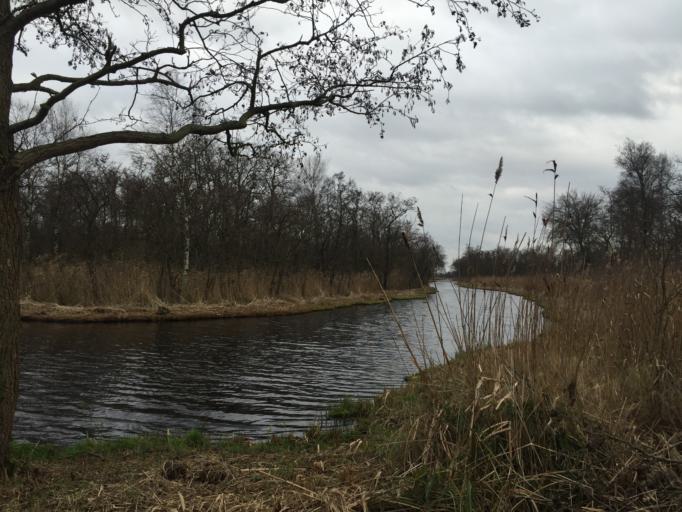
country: NL
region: North Holland
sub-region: Gemeente Wijdemeren
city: Kortenhoef
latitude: 52.2693
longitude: 5.0924
